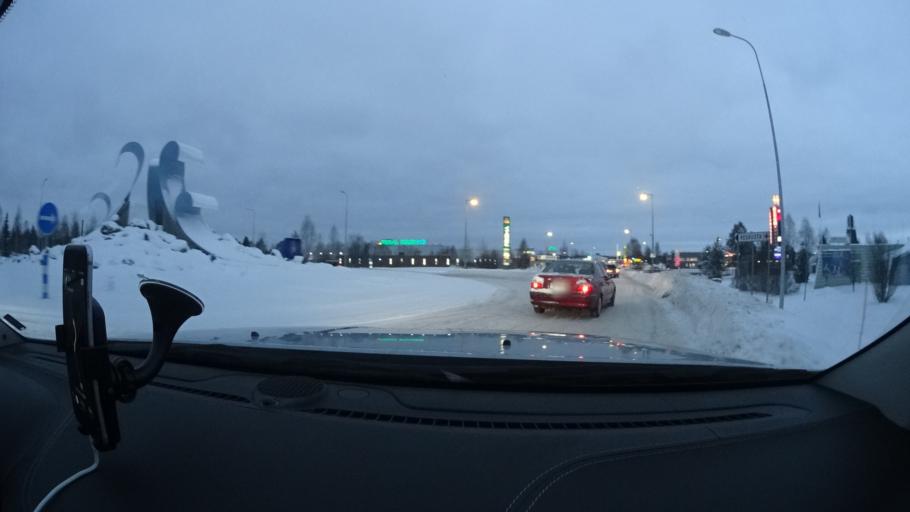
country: FI
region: Northern Ostrobothnia
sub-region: Koillismaa
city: Kuusamo
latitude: 65.9558
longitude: 29.1566
